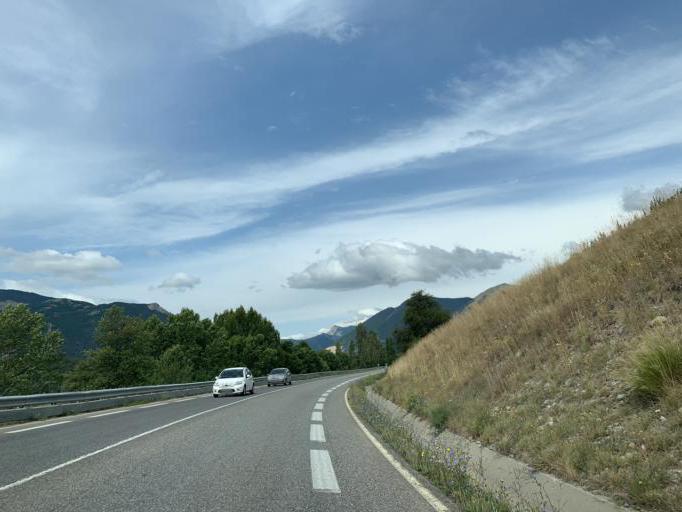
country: FR
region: Provence-Alpes-Cote d'Azur
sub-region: Departement des Hautes-Alpes
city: La Roche-des-Arnauds
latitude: 44.5453
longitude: 5.9888
